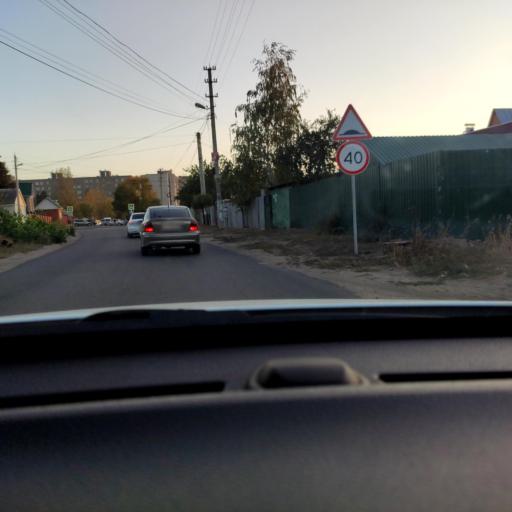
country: RU
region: Voronezj
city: Voronezh
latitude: 51.7010
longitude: 39.2688
